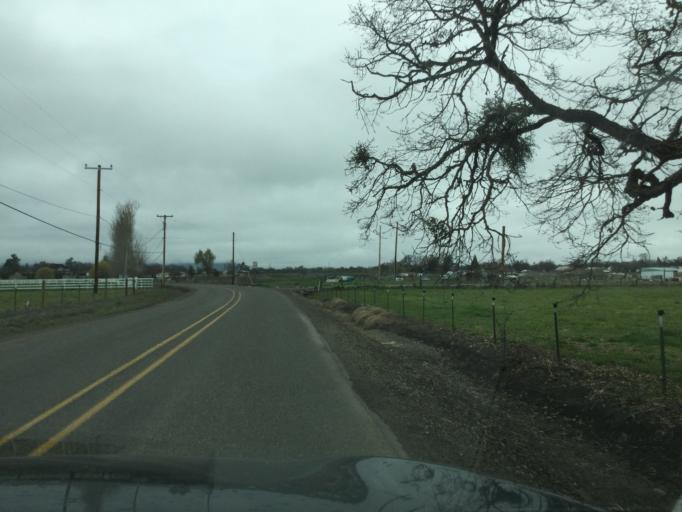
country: US
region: Oregon
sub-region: Jackson County
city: Central Point
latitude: 42.4031
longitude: -122.9092
